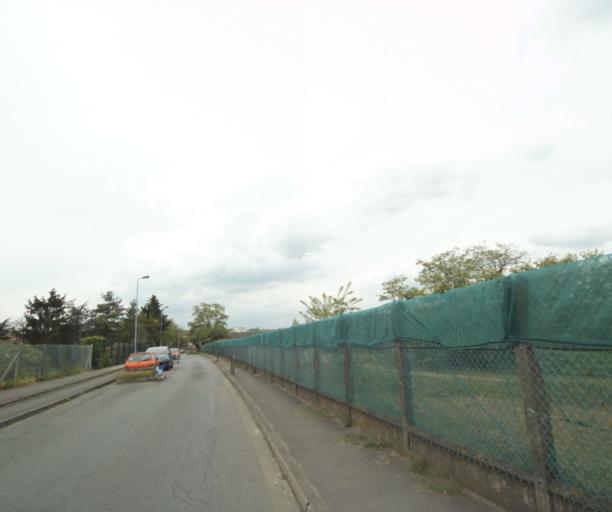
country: FR
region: Ile-de-France
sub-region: Departement des Yvelines
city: Les Mureaux
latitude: 48.9931
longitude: 1.9202
